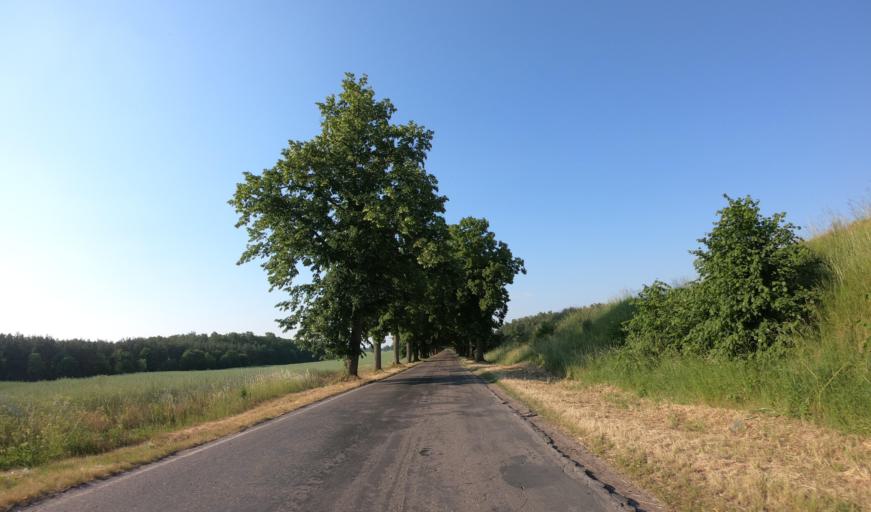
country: PL
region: West Pomeranian Voivodeship
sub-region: Powiat lobeski
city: Dobra
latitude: 53.5603
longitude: 15.3049
